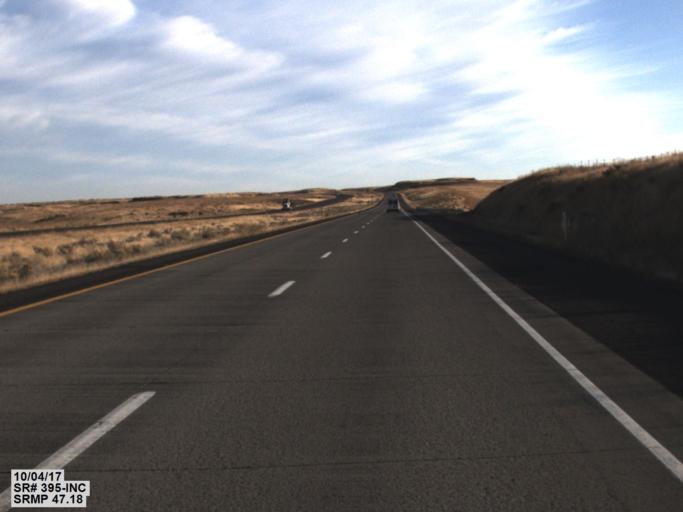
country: US
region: Washington
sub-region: Franklin County
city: Connell
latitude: 46.5804
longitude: -118.9741
